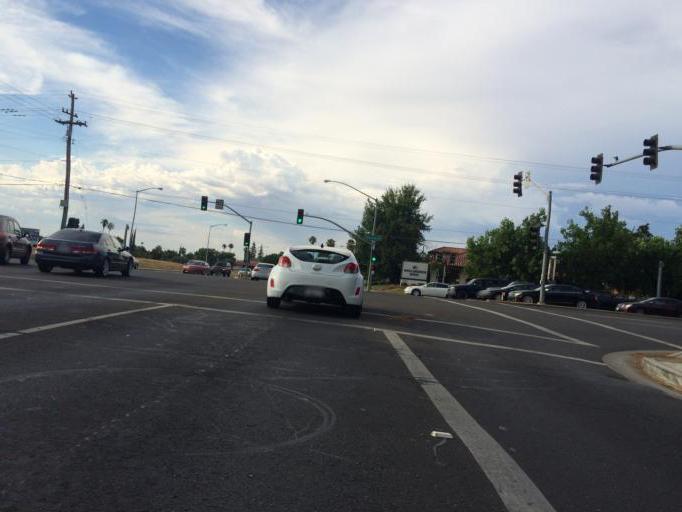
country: US
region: California
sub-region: Fresno County
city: Clovis
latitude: 36.8370
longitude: -119.7721
